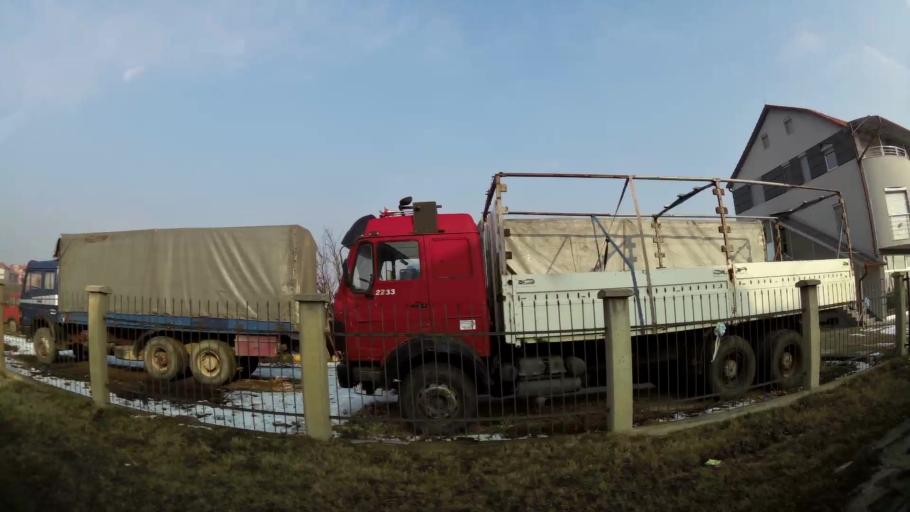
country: MK
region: Ilinden
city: Marino
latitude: 41.9822
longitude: 21.5962
